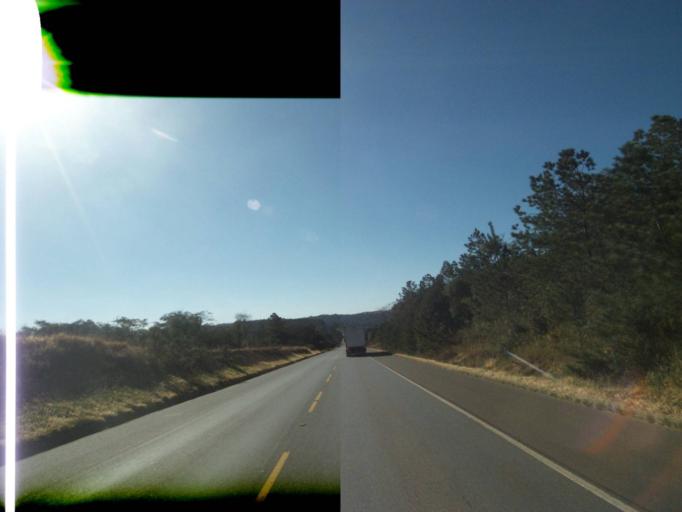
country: BR
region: Parana
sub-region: Tibagi
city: Tibagi
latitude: -24.5952
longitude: -50.4374
